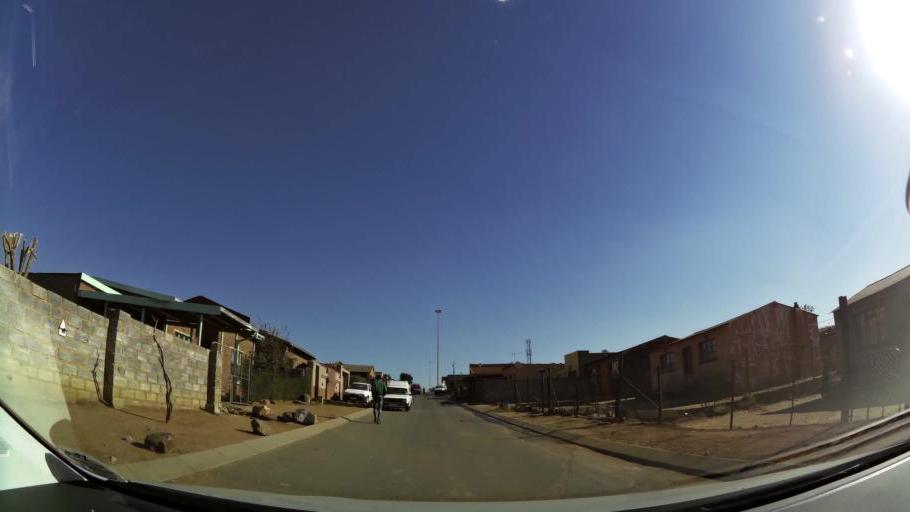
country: ZA
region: Gauteng
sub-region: Ekurhuleni Metropolitan Municipality
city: Tembisa
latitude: -26.0181
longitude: 28.2388
